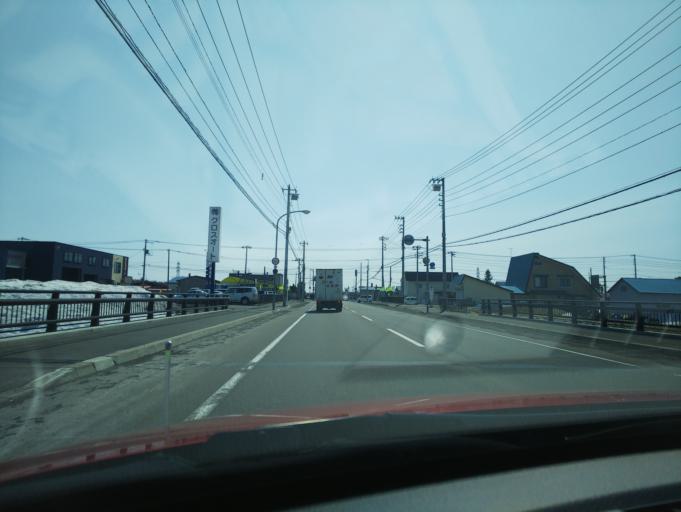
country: JP
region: Hokkaido
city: Nayoro
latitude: 44.3372
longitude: 142.4643
